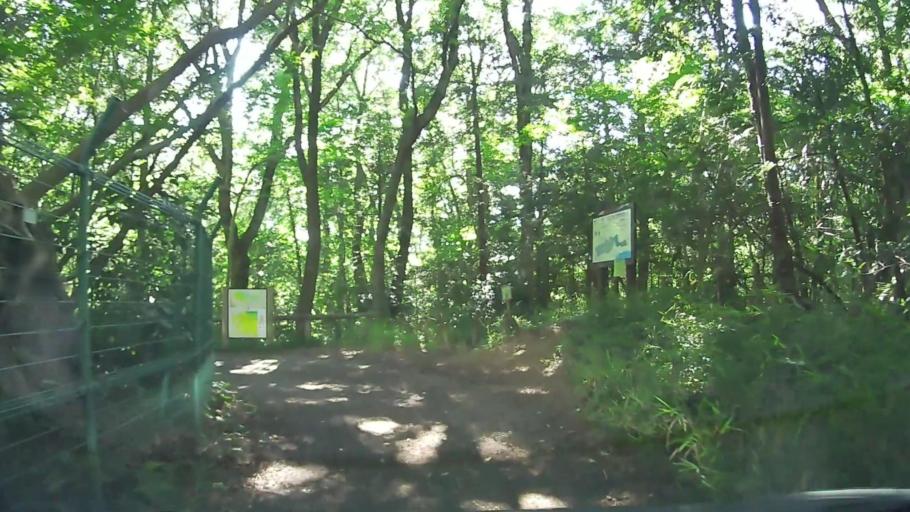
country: JP
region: Tokyo
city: Fussa
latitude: 35.7815
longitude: 139.3706
